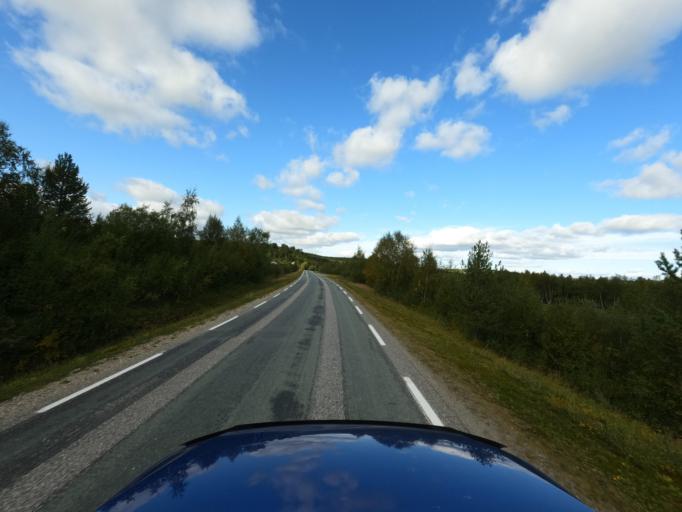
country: NO
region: Finnmark Fylke
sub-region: Karasjok
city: Karasjohka
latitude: 69.4128
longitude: 25.8021
